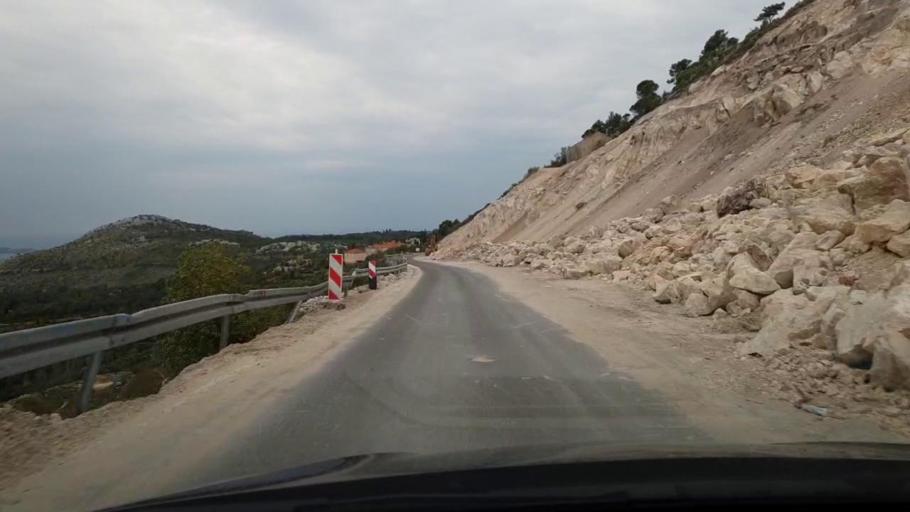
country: HR
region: Dubrovacko-Neretvanska
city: Cibaca
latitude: 42.6513
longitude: 18.1593
